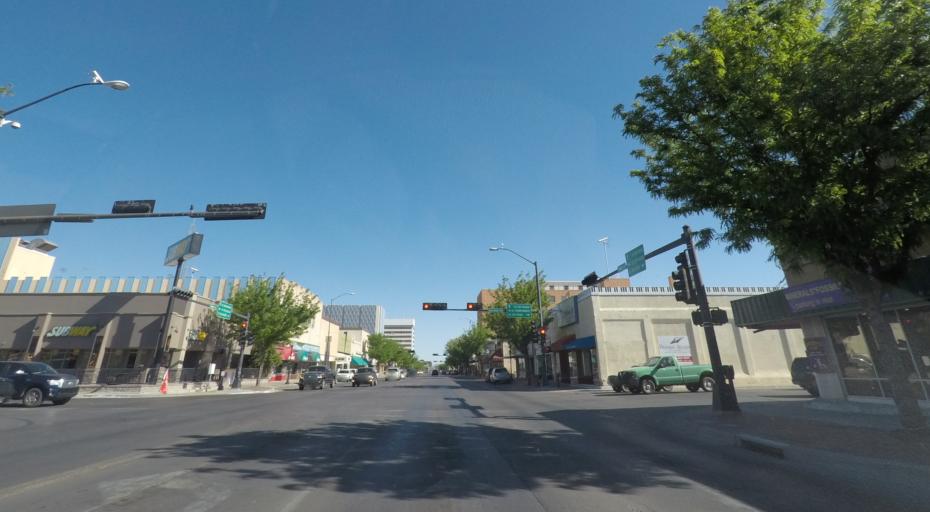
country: US
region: New Mexico
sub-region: Chaves County
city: Roswell
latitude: 33.3940
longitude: -104.5228
